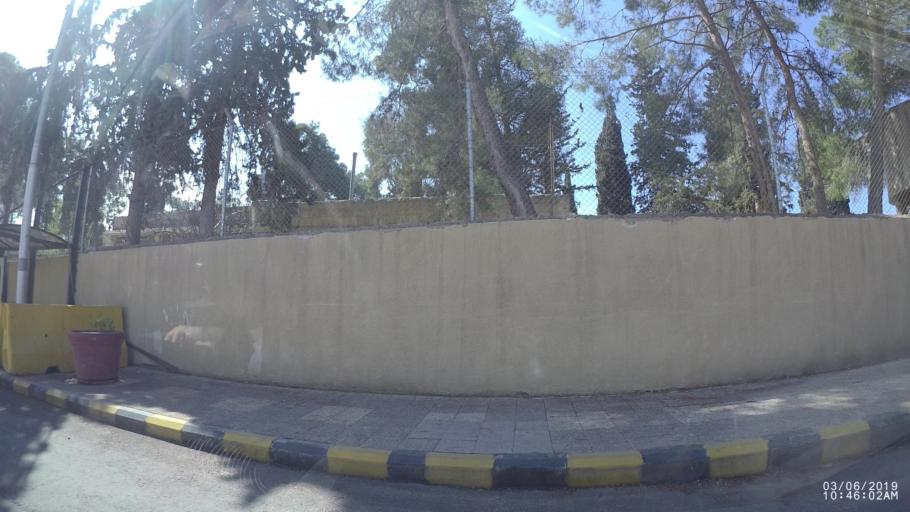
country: JO
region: Amman
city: Amman
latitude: 31.9768
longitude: 35.9820
